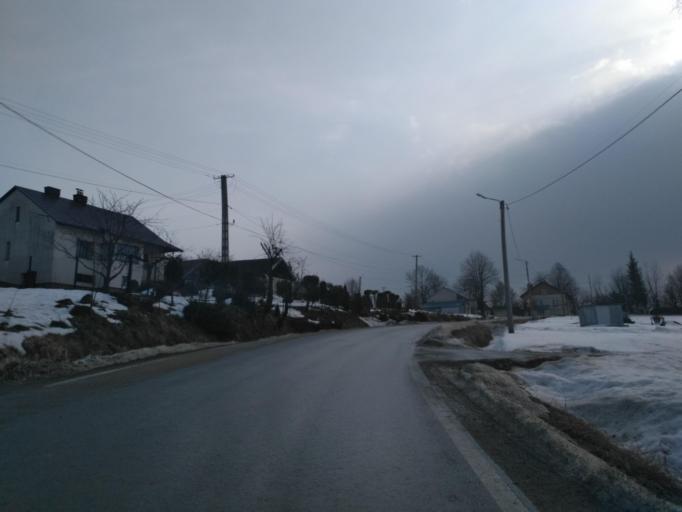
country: PL
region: Subcarpathian Voivodeship
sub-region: Powiat brzozowski
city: Dydnia
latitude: 49.6494
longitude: 22.1600
